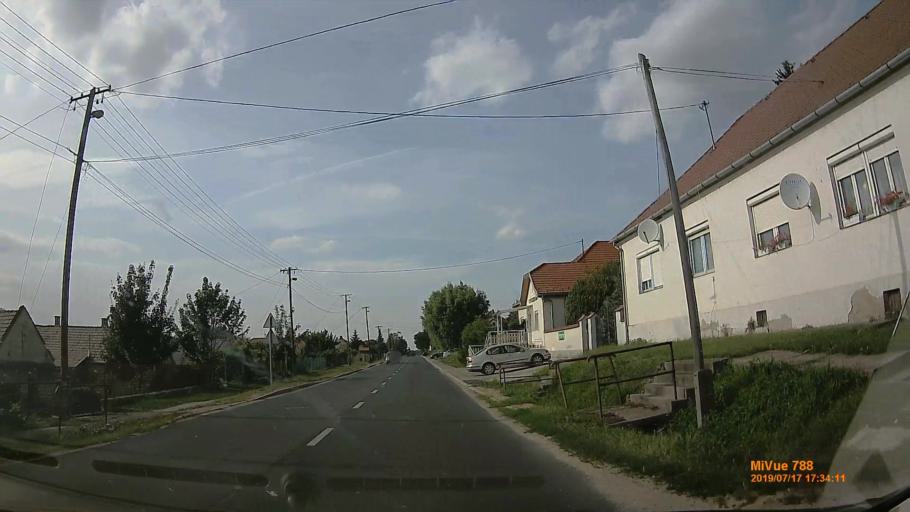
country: HU
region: Veszprem
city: Ajka
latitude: 47.0546
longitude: 17.5555
